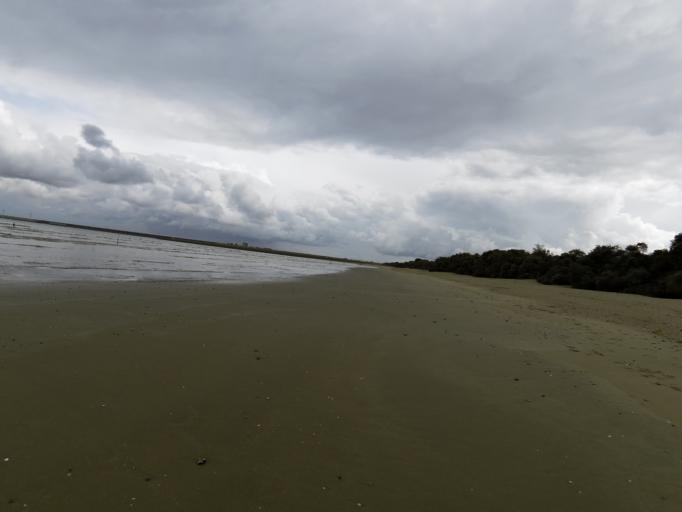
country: NL
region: South Holland
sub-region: Gemeente Goeree-Overflakkee
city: Goedereede
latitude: 51.8319
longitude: 4.0202
